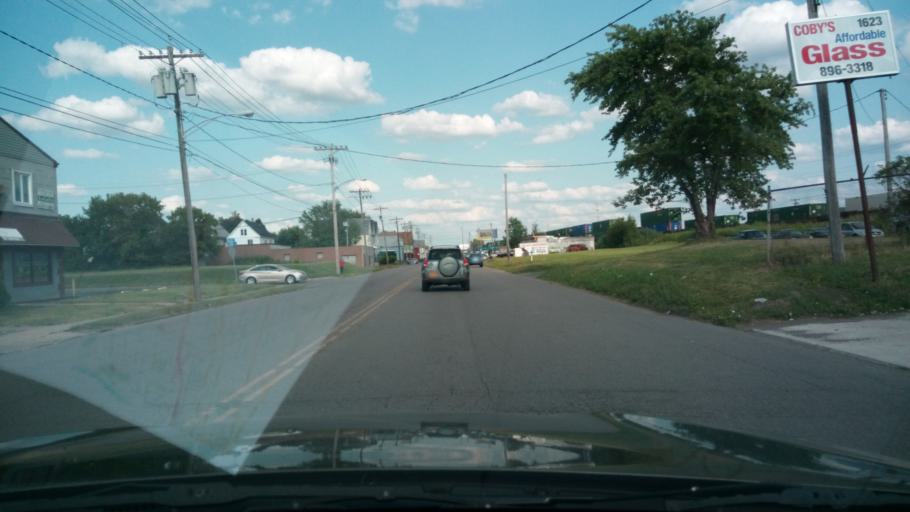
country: US
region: New York
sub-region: Erie County
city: Sloan
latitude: 42.8847
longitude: -78.8104
